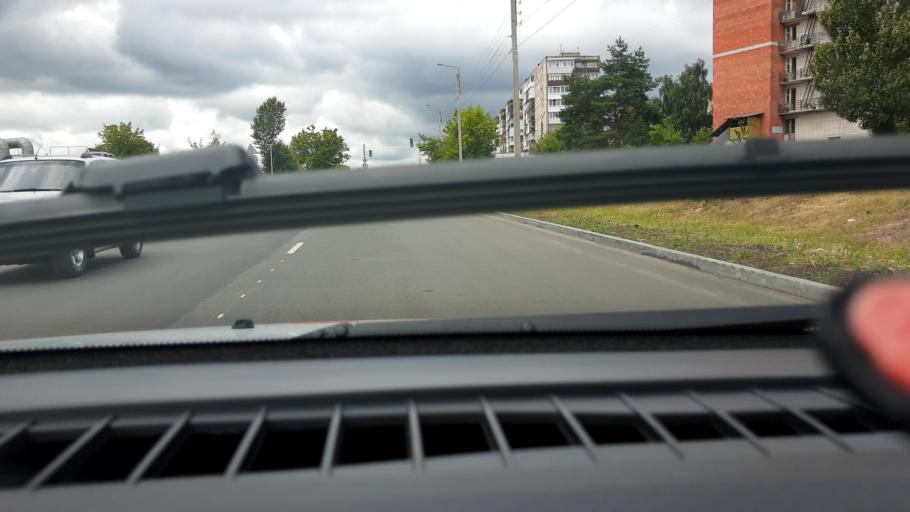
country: RU
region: Nizjnij Novgorod
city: Dzerzhinsk
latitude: 56.2216
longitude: 43.4088
